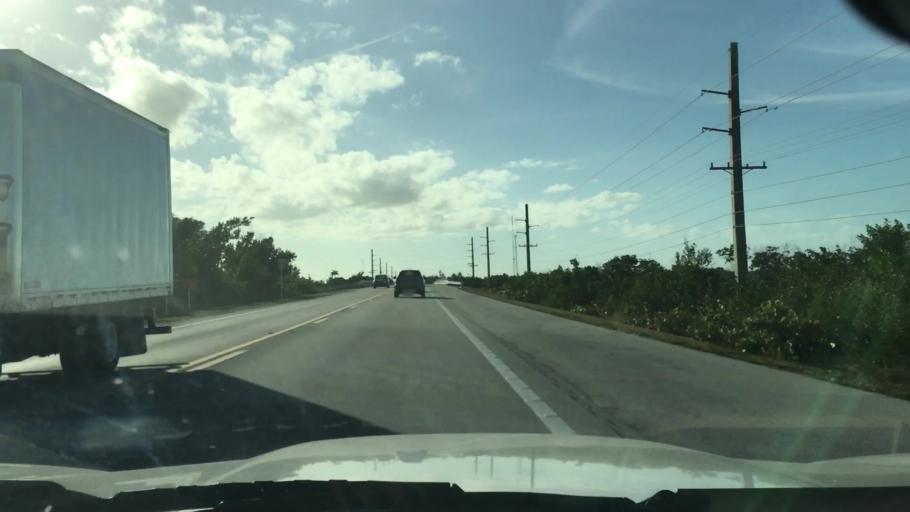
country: US
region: Florida
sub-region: Monroe County
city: Big Pine Key
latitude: 24.6636
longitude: -81.4004
